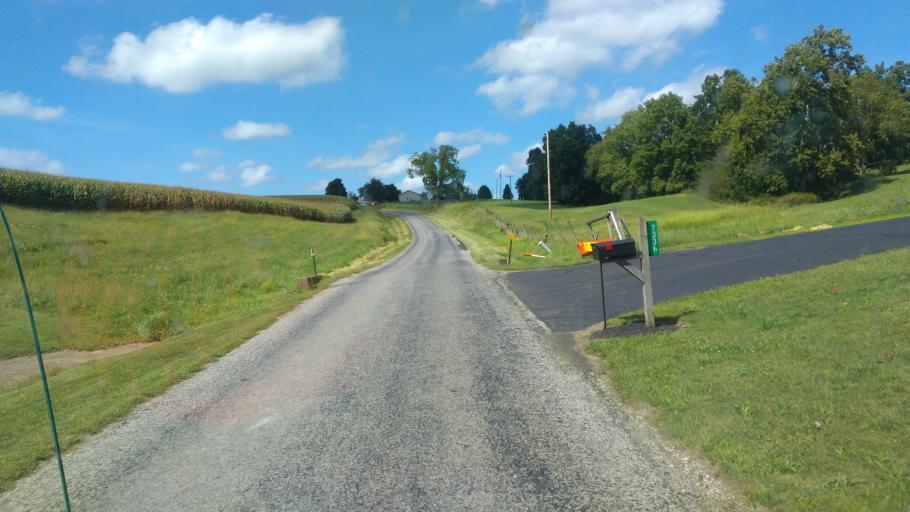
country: US
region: Ohio
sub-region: Holmes County
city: Millersburg
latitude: 40.6128
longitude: -81.8478
